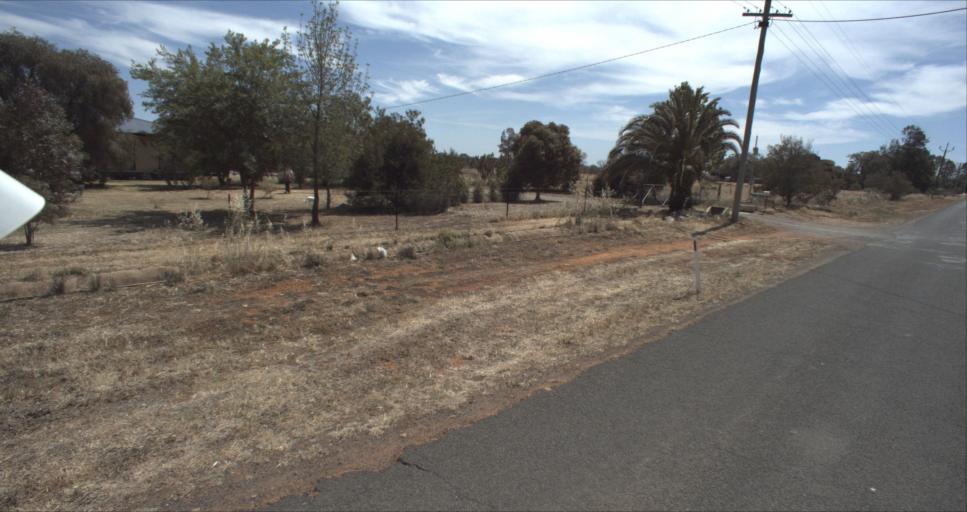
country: AU
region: New South Wales
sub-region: Leeton
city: Leeton
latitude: -34.5964
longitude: 146.4278
